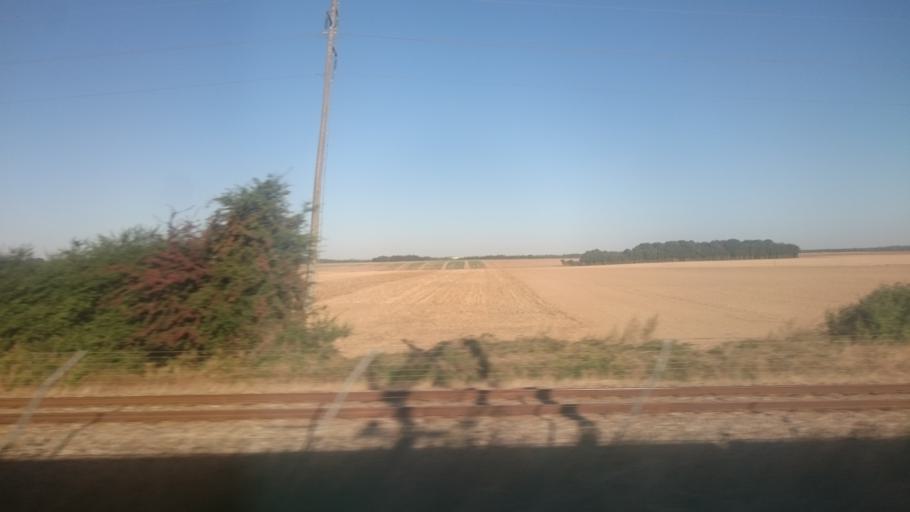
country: FR
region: Centre
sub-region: Departement d'Eure-et-Loir
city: Beville-le-Comte
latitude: 48.4152
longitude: 1.7531
